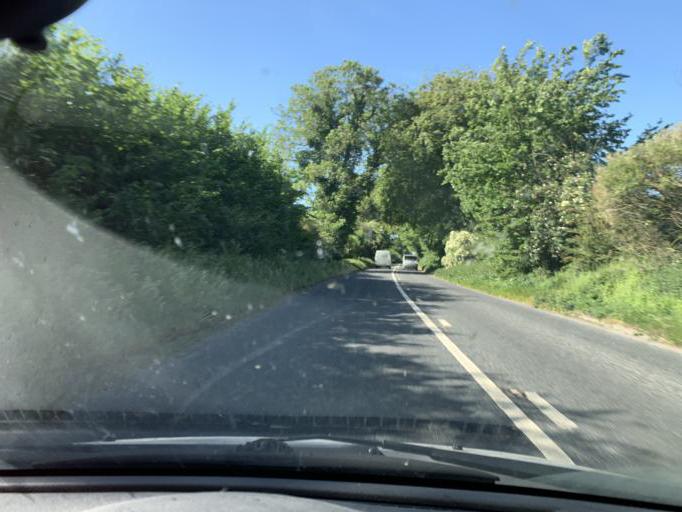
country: GB
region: England
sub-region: Wiltshire
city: Durnford
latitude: 51.1112
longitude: -1.7918
